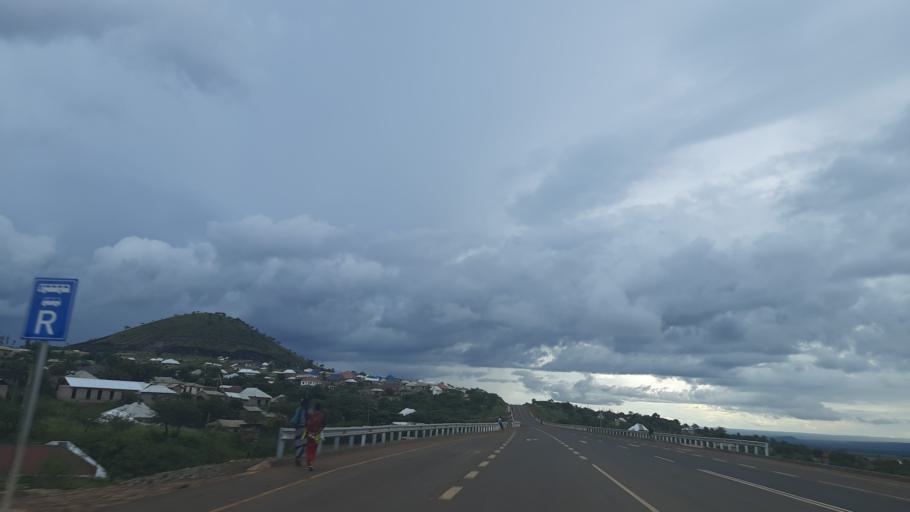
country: TZ
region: Arusha
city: Arusha
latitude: -3.4369
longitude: 36.6440
